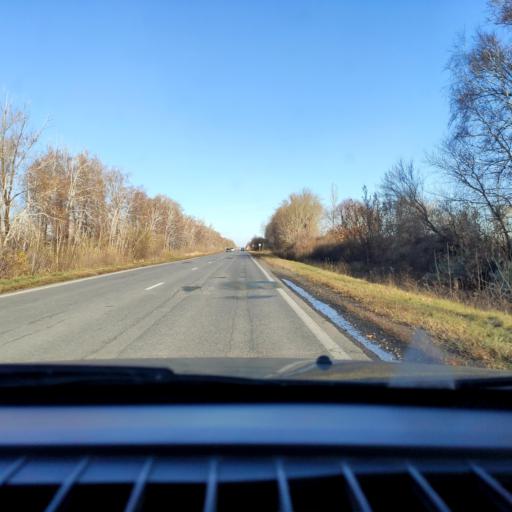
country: RU
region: Samara
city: Tol'yatti
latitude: 53.6122
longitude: 49.3151
